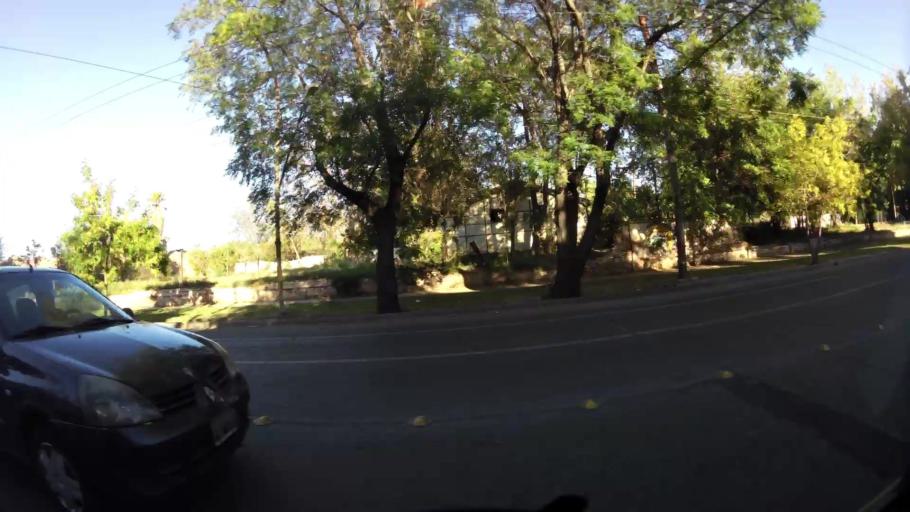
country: AR
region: Mendoza
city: Mendoza
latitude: -32.8799
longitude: -68.8460
